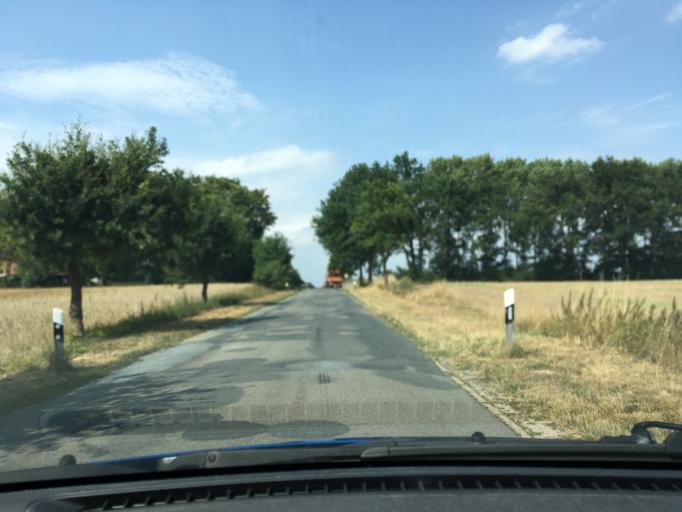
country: DE
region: Lower Saxony
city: Natendorf
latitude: 53.1127
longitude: 10.4475
